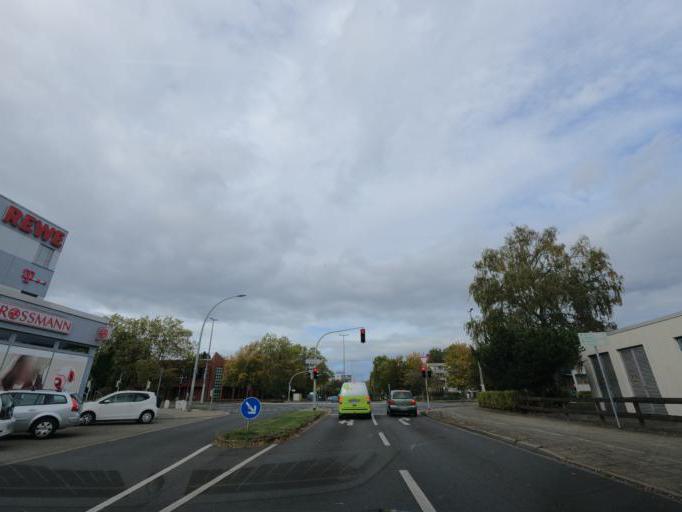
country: DE
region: Lower Saxony
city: Braunschweig
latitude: 52.2488
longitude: 10.4804
